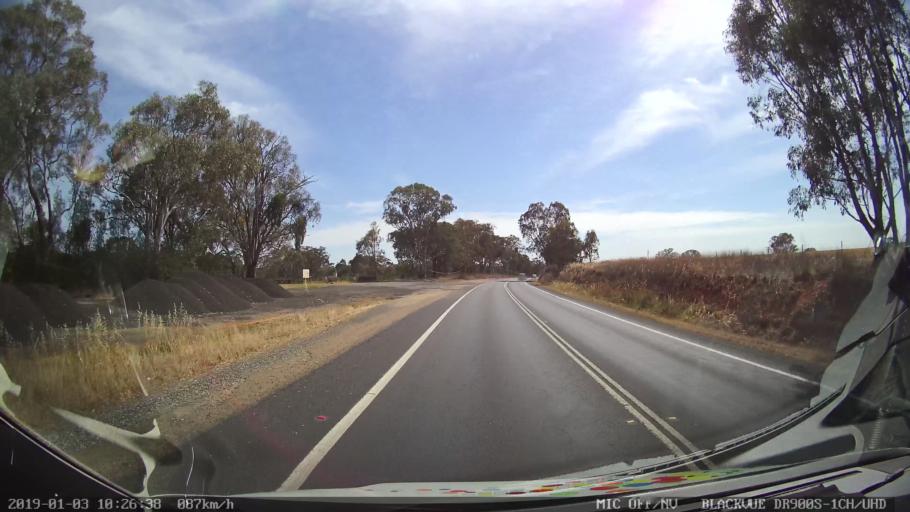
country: AU
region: New South Wales
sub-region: Young
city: Young
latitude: -34.4105
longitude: 148.2509
